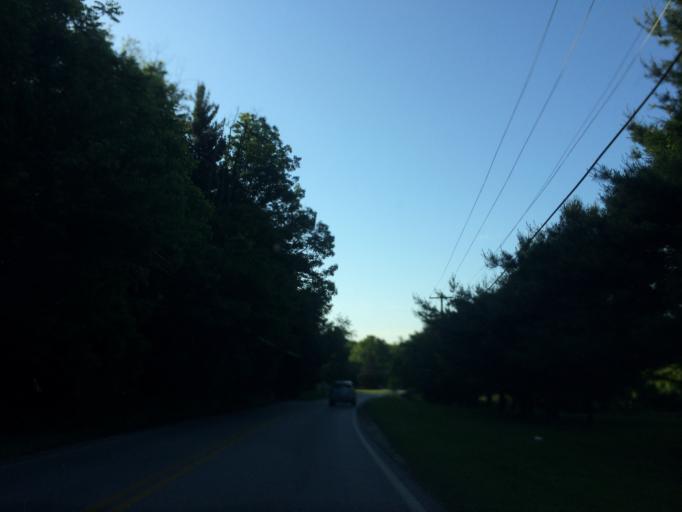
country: US
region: Maryland
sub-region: Howard County
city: Highland
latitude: 39.2631
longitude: -76.9754
